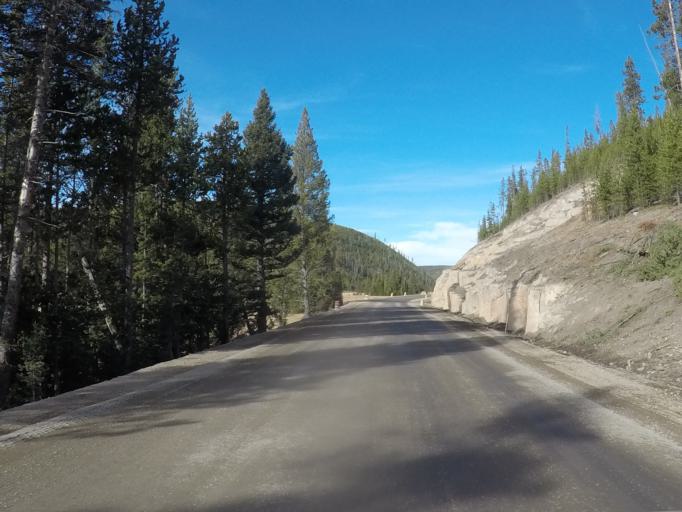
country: US
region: Montana
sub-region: Gallatin County
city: West Yellowstone
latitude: 44.8144
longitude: -110.7296
